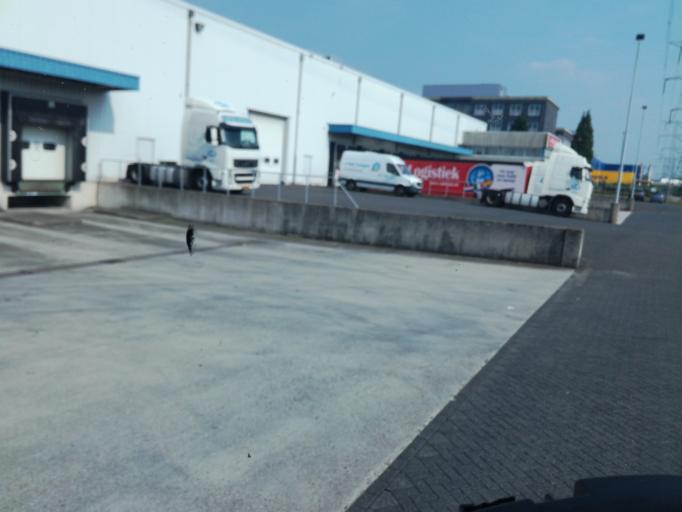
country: NL
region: North Brabant
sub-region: Gemeente Son en Breugel
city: Son
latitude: 51.5036
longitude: 5.4691
